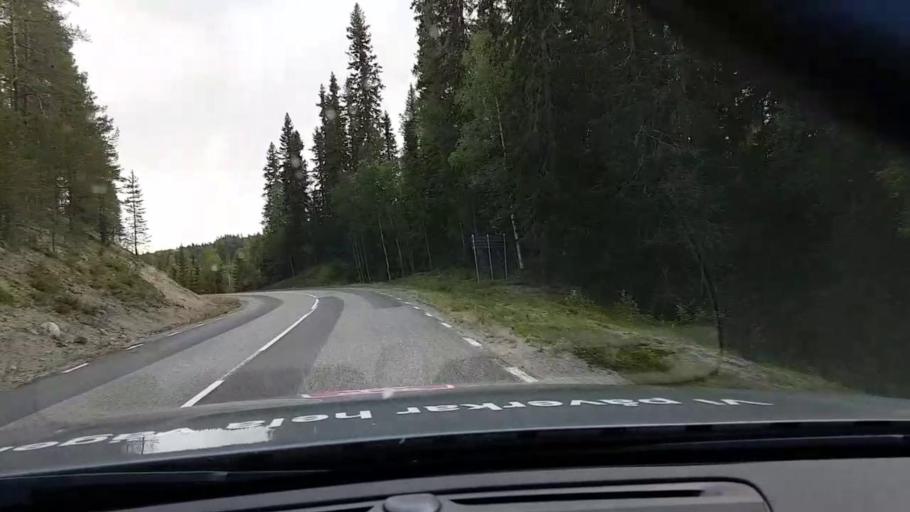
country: SE
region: Vaesterbotten
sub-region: Asele Kommun
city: Asele
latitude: 63.8379
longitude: 17.4343
